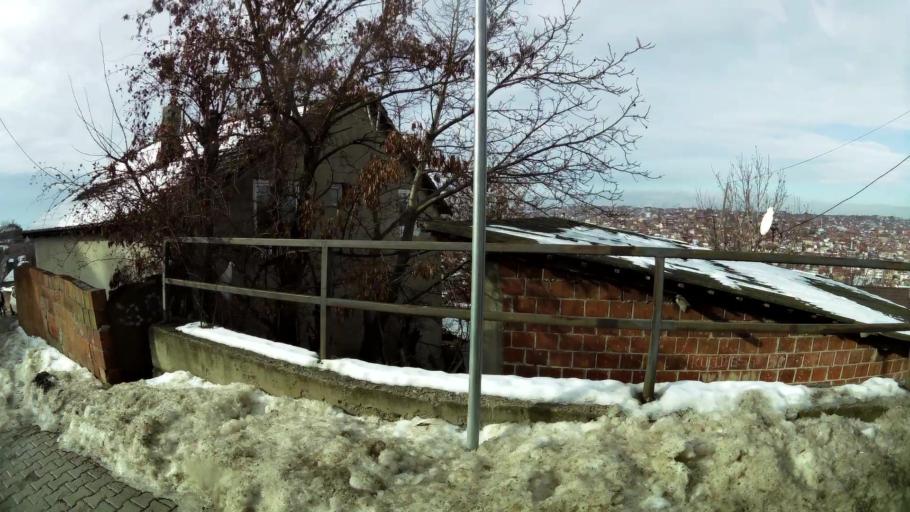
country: XK
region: Pristina
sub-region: Komuna e Prishtines
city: Pristina
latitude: 42.6747
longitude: 21.1761
